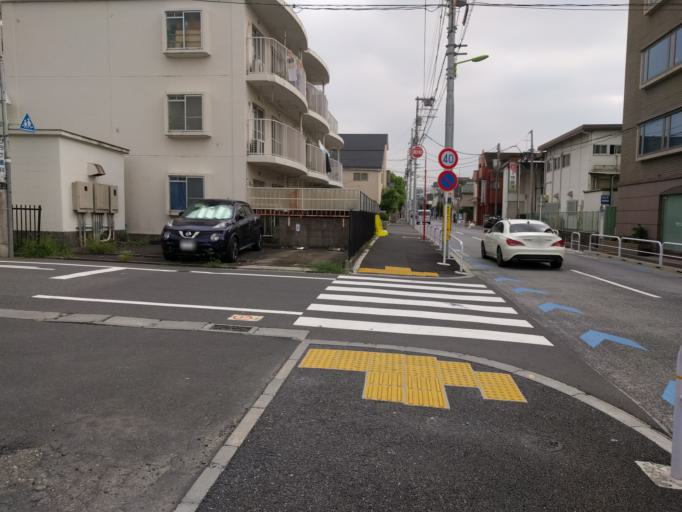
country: JP
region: Tokyo
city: Tokyo
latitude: 35.6057
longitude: 139.6577
